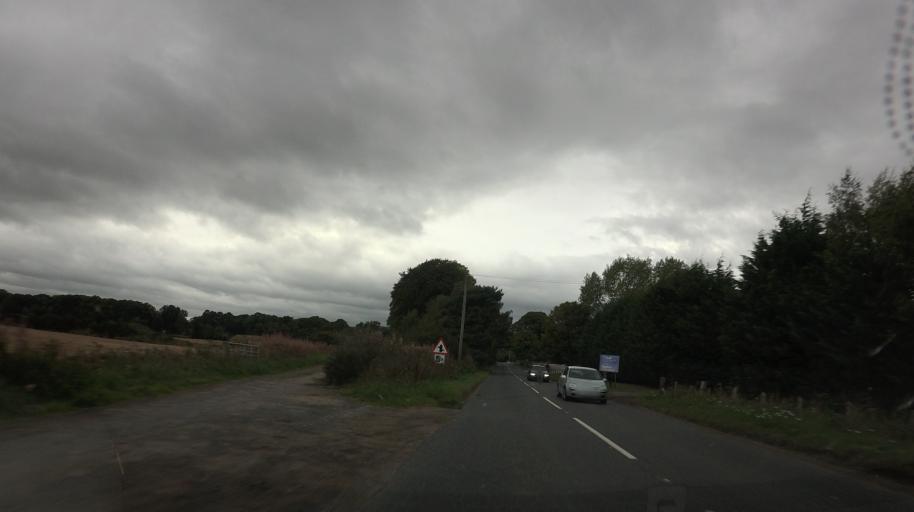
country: GB
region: Scotland
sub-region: Aberdeenshire
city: Kemnay
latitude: 57.1830
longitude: -2.4794
